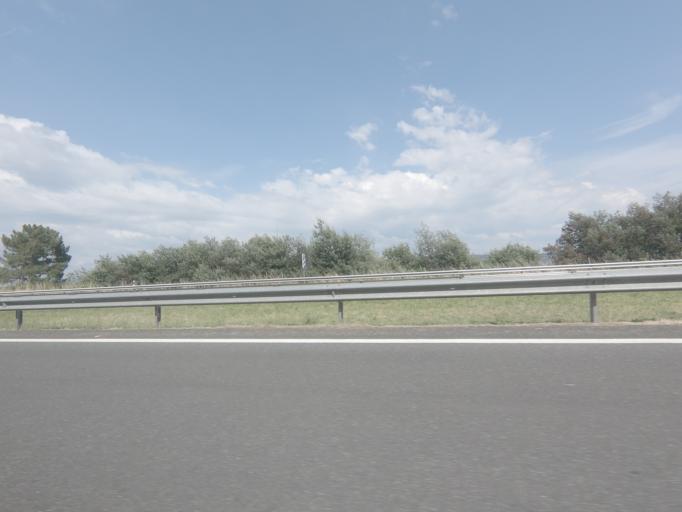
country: ES
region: Galicia
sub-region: Provincia de Ourense
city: Ourense
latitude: 42.3370
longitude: -7.8854
